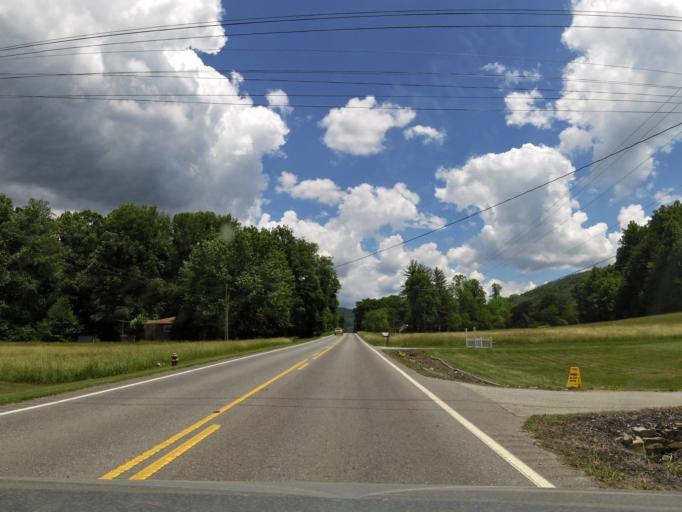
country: US
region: North Carolina
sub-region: Graham County
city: Robbinsville
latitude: 35.2952
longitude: -83.7900
